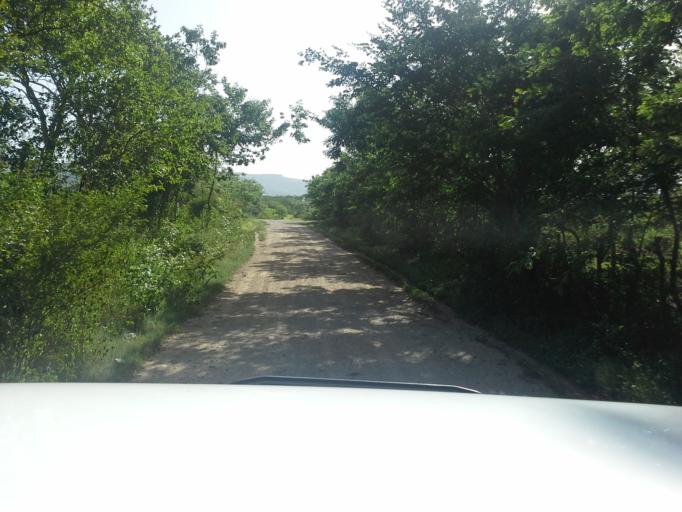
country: NI
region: Matagalpa
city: Ciudad Dario
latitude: 12.6618
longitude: -86.0665
